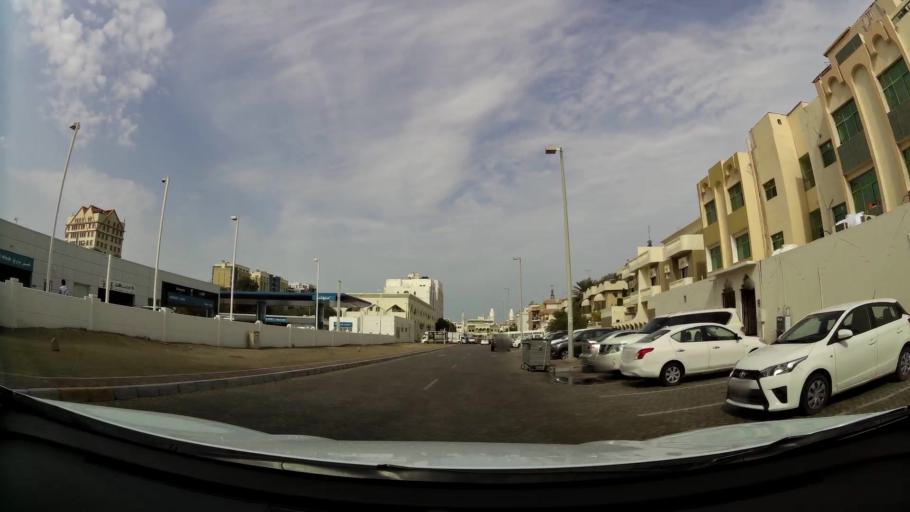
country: AE
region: Abu Dhabi
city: Abu Dhabi
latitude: 24.4396
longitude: 54.4143
